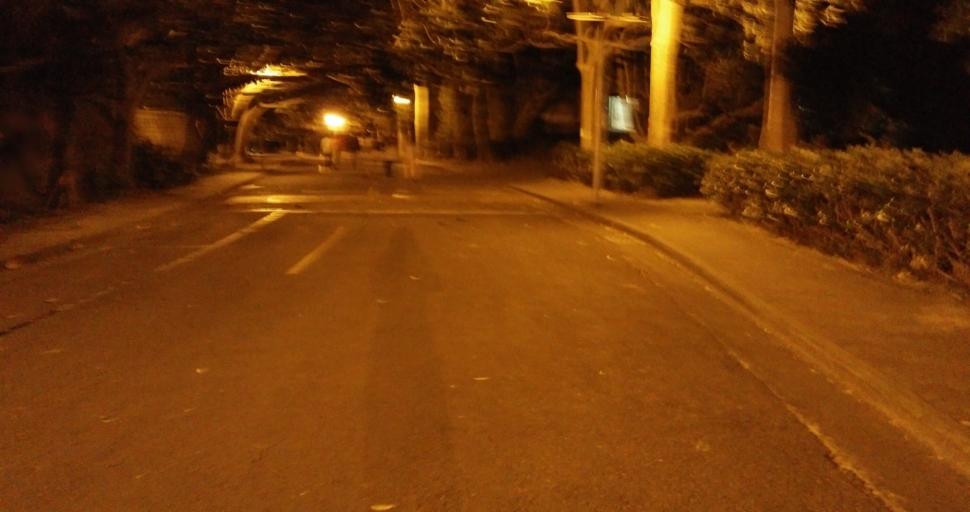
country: TW
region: Taiwan
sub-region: Hsinchu
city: Hsinchu
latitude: 24.7579
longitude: 120.9523
